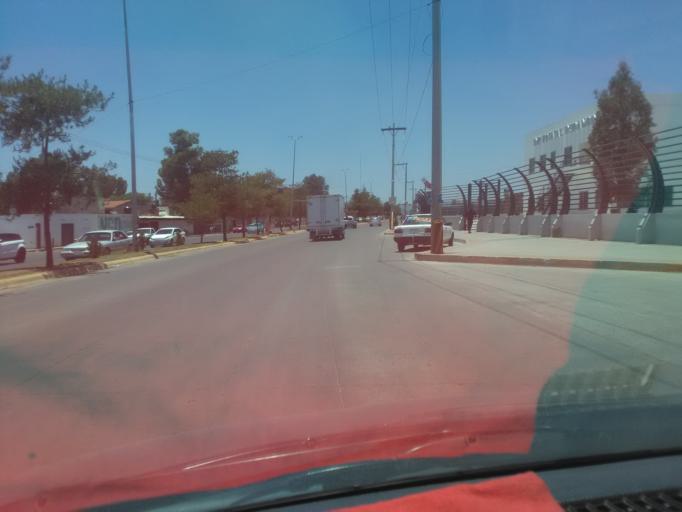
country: MX
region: Durango
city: Victoria de Durango
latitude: 24.0453
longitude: -104.6543
